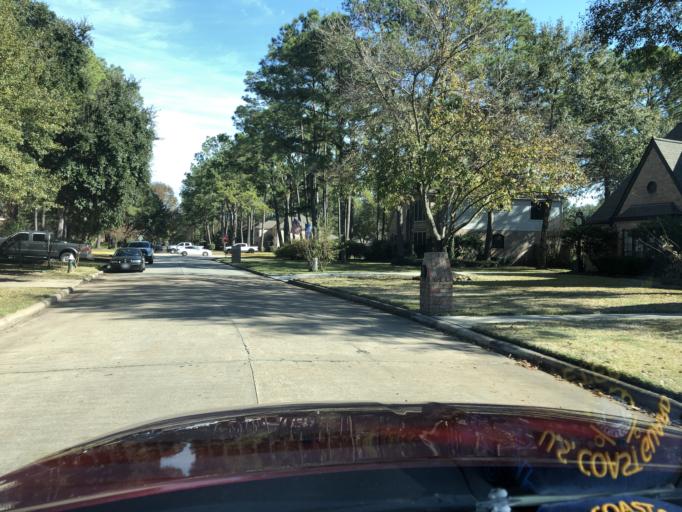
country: US
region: Texas
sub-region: Harris County
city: Tomball
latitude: 30.0196
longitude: -95.5471
